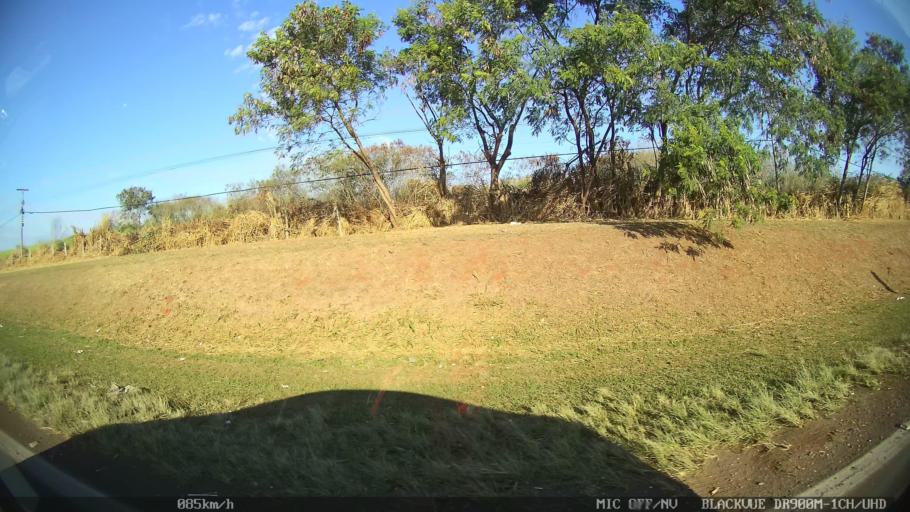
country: BR
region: Sao Paulo
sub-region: Piracicaba
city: Piracicaba
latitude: -22.6656
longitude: -47.6200
